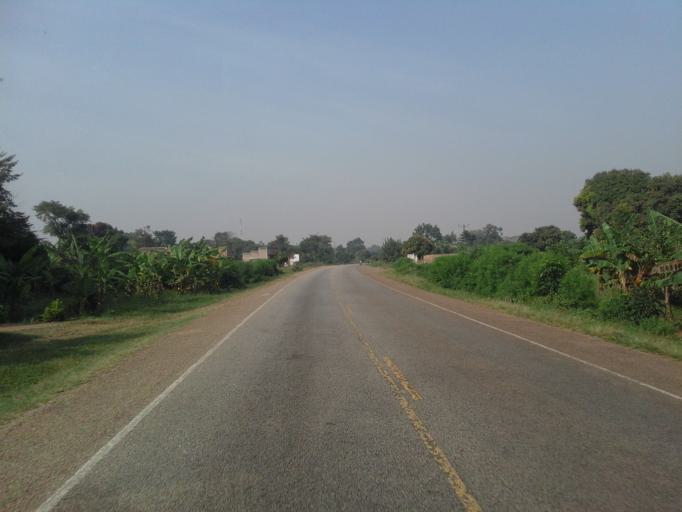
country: UG
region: Eastern Region
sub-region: Budaka District
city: Budaka
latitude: 1.0230
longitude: 33.9735
